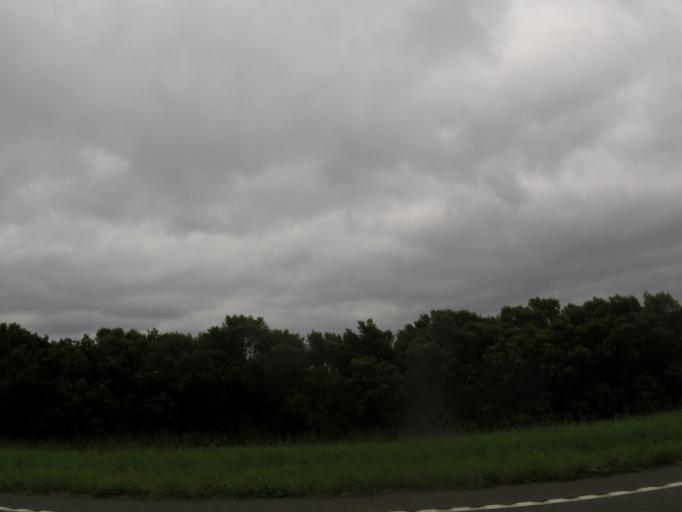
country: US
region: Georgia
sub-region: Glynn County
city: Brunswick
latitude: 31.0834
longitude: -81.4755
